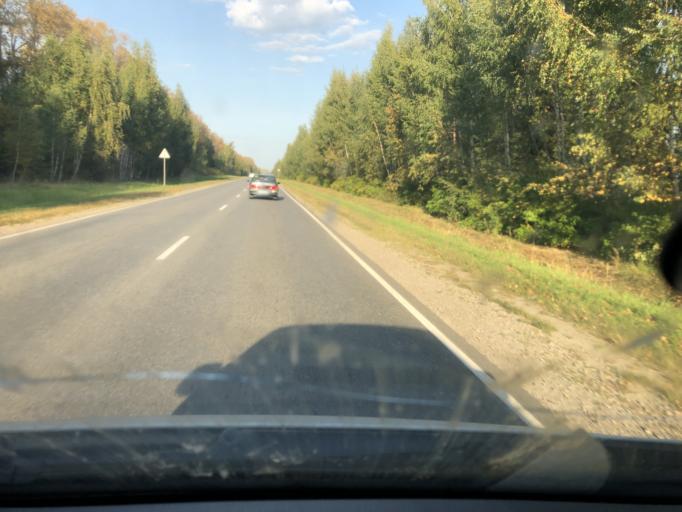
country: RU
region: Kaluga
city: Peremyshl'
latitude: 54.2439
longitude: 36.0826
